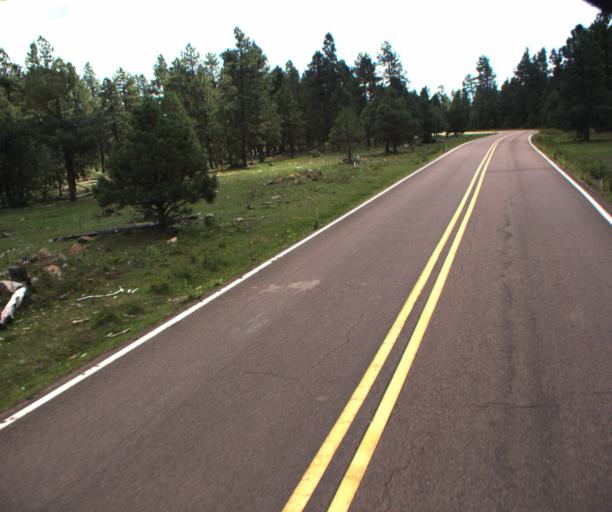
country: US
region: Arizona
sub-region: Navajo County
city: Pinetop-Lakeside
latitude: 34.0090
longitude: -109.7706
